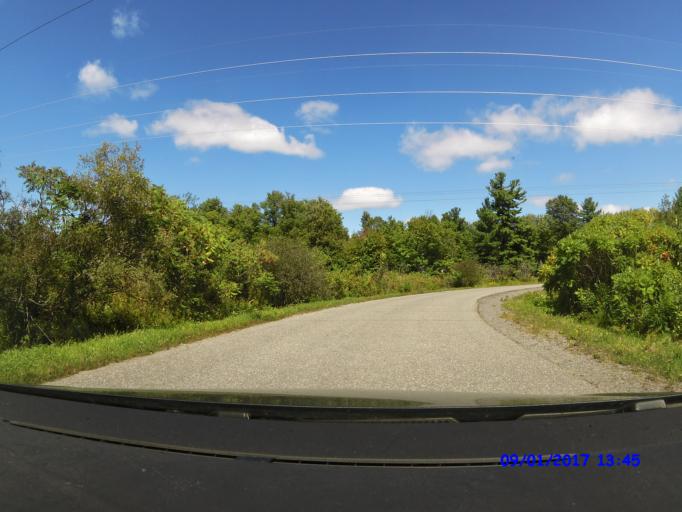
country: CA
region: Ontario
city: Bells Corners
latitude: 45.3630
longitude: -75.9764
